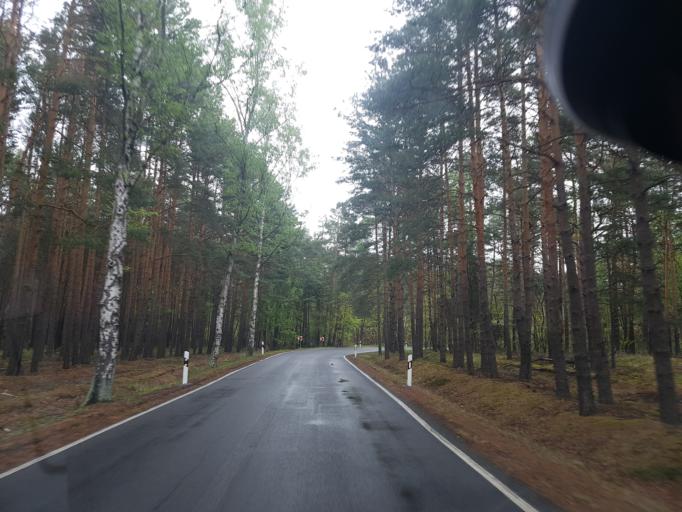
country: DE
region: Brandenburg
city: Spremberg
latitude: 51.6315
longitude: 14.4286
